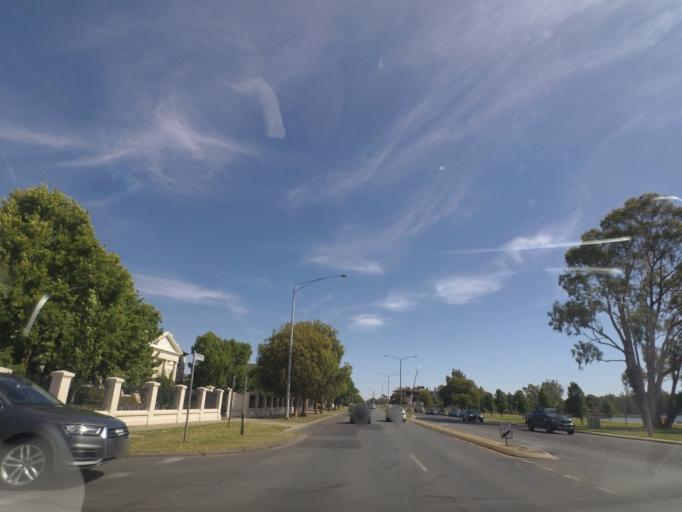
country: AU
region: Victoria
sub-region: Greater Shepparton
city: Shepparton
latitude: -36.3877
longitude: 145.3980
